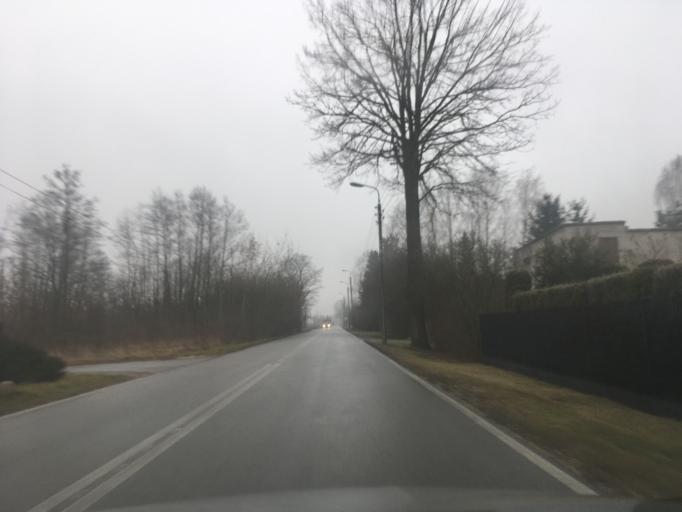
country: PL
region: Masovian Voivodeship
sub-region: Powiat piaseczynski
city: Lesznowola
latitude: 52.0544
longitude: 20.9051
